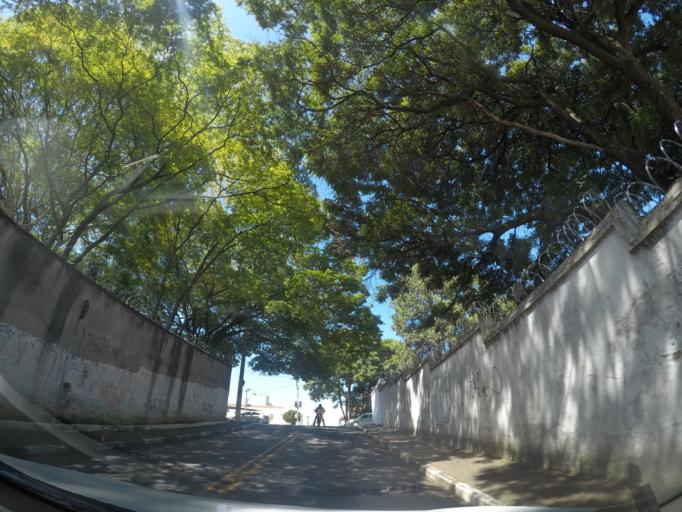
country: BR
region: Sao Paulo
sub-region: Guarulhos
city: Guarulhos
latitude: -23.4538
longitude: -46.5416
